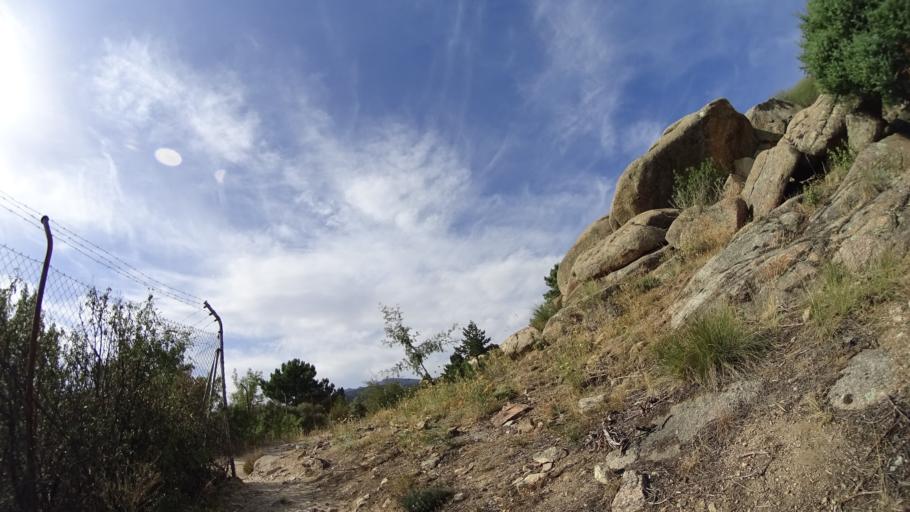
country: ES
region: Madrid
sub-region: Provincia de Madrid
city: Becerril de la Sierra
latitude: 40.7160
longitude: -4.0028
